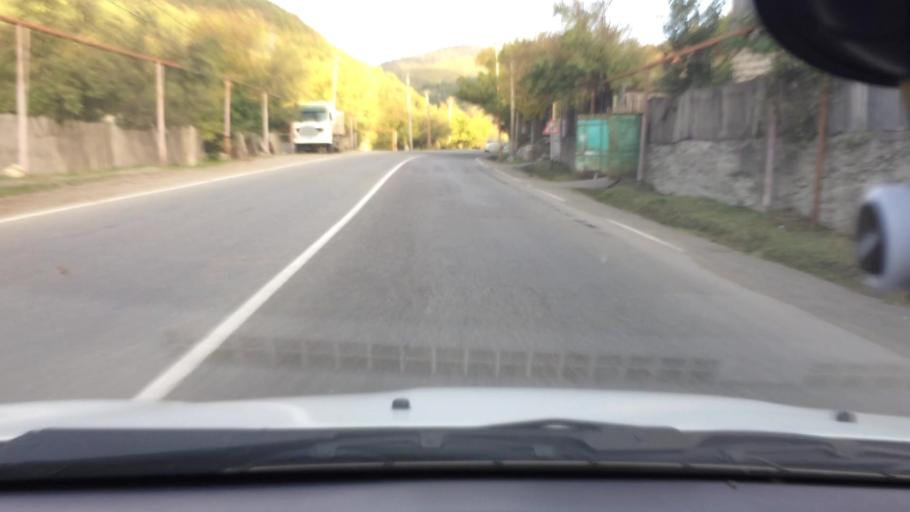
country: GE
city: Surami
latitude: 42.0327
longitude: 43.5226
